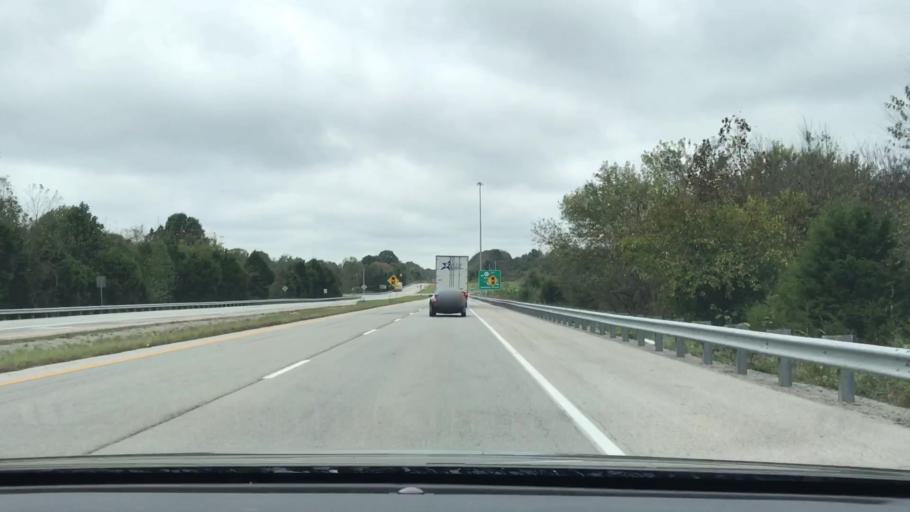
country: US
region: Kentucky
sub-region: Pulaski County
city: Somerset
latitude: 37.0962
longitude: -84.6578
